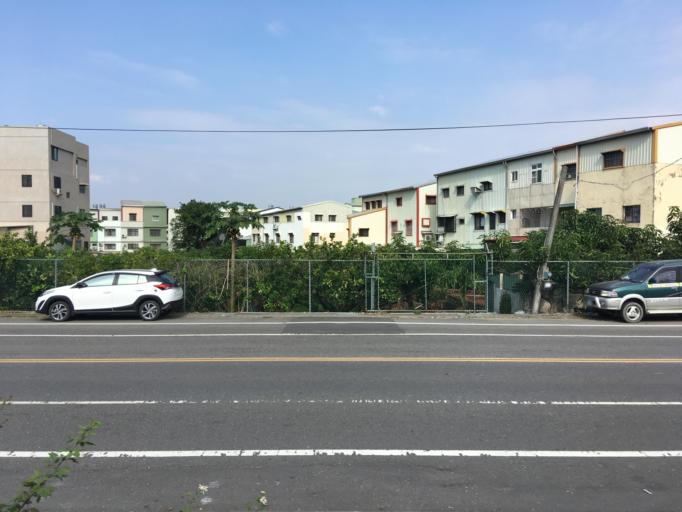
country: TW
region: Taiwan
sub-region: Chiayi
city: Jiayi Shi
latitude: 23.4937
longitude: 120.4999
